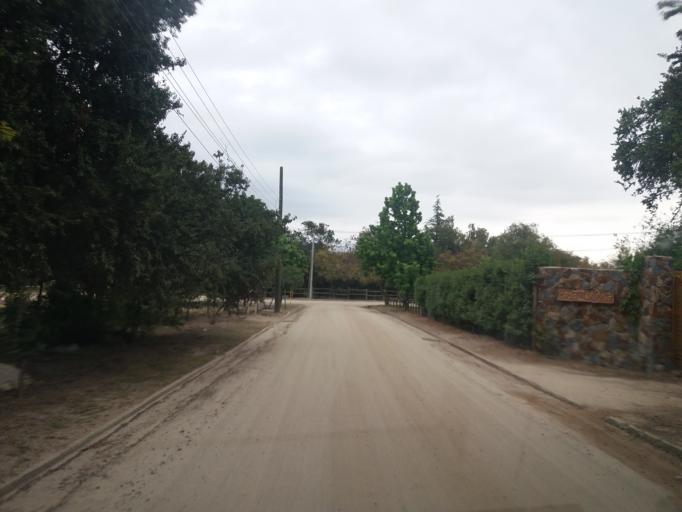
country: CL
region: Valparaiso
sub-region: Provincia de Marga Marga
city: Limache
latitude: -33.0269
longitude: -71.1385
